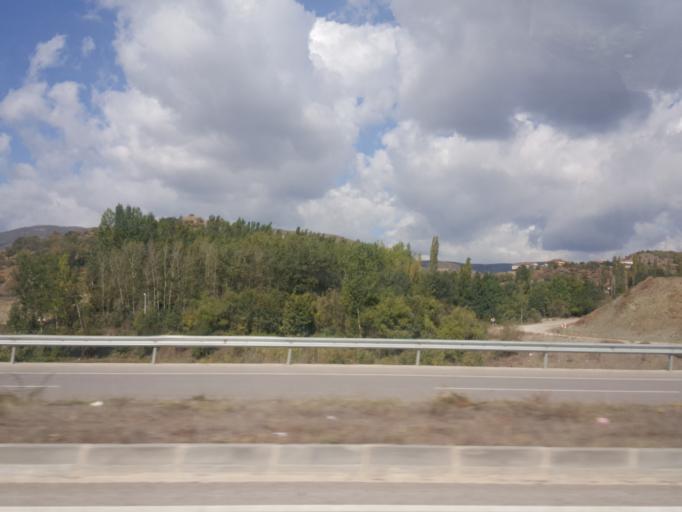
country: TR
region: Tokat
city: Gokdere
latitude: 40.3768
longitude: 36.6767
